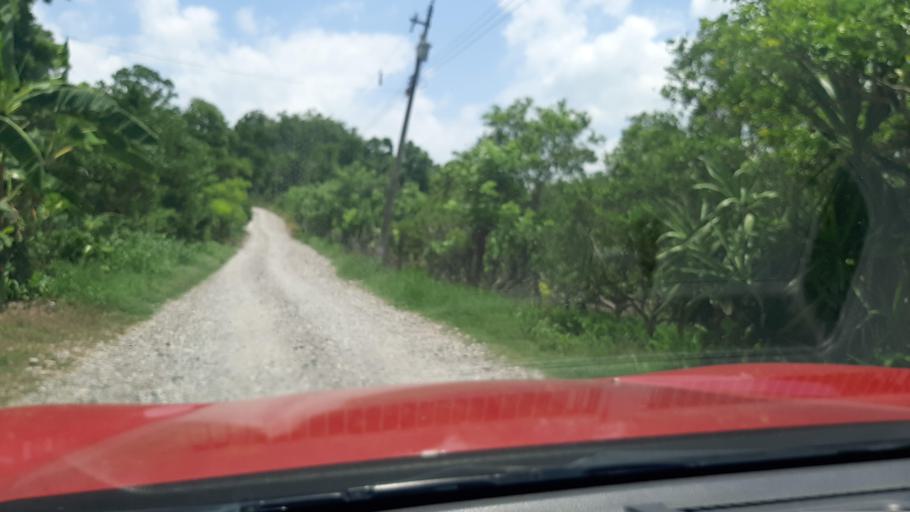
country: MX
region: Veracruz
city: Papantla de Olarte
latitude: 20.4304
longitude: -97.2645
